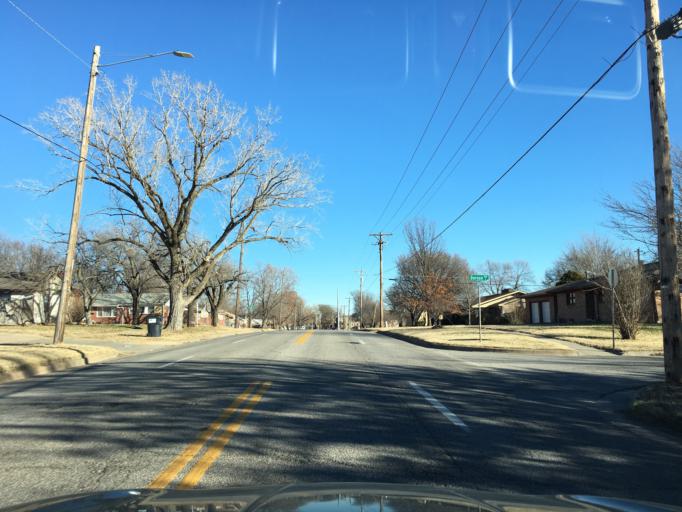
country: US
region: Kansas
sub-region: Sedgwick County
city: Wichita
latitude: 37.6720
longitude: -97.2483
